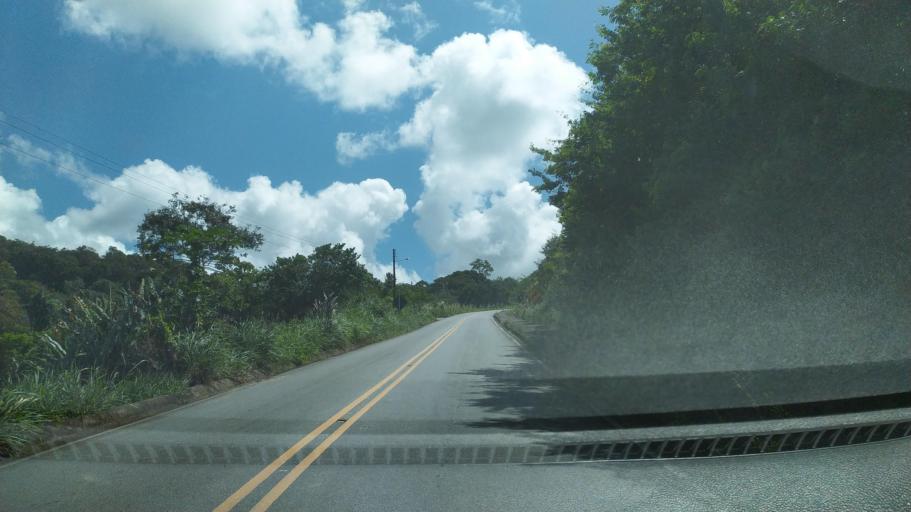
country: BR
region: Alagoas
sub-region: Uniao Dos Palmares
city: Uniao dos Palmares
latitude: -9.1650
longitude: -36.0675
